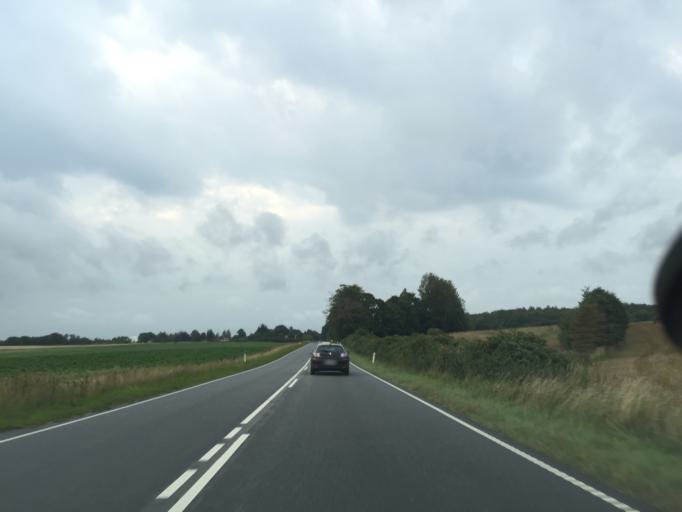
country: DK
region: Central Jutland
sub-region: Skanderborg Kommune
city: Galten
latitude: 56.1036
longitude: 9.8939
